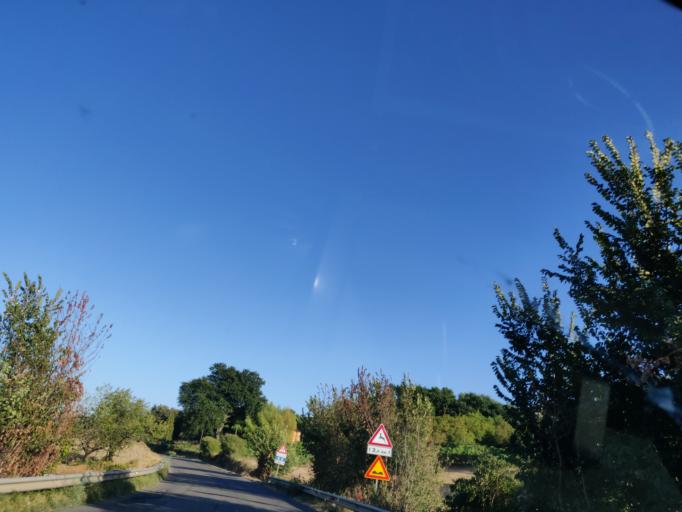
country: IT
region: Latium
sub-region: Provincia di Viterbo
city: Acquapendente
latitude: 42.7623
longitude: 11.8570
